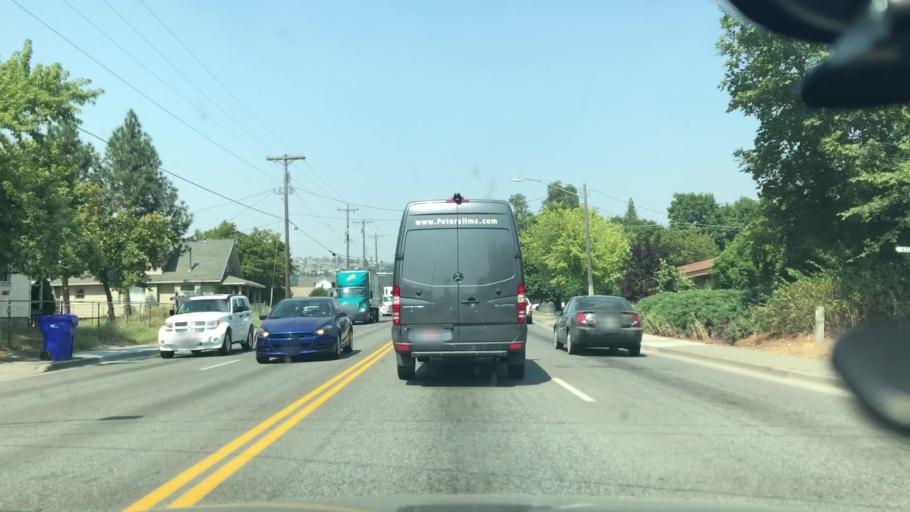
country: US
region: Washington
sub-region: Spokane County
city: Millwood
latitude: 47.6958
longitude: -117.2828
